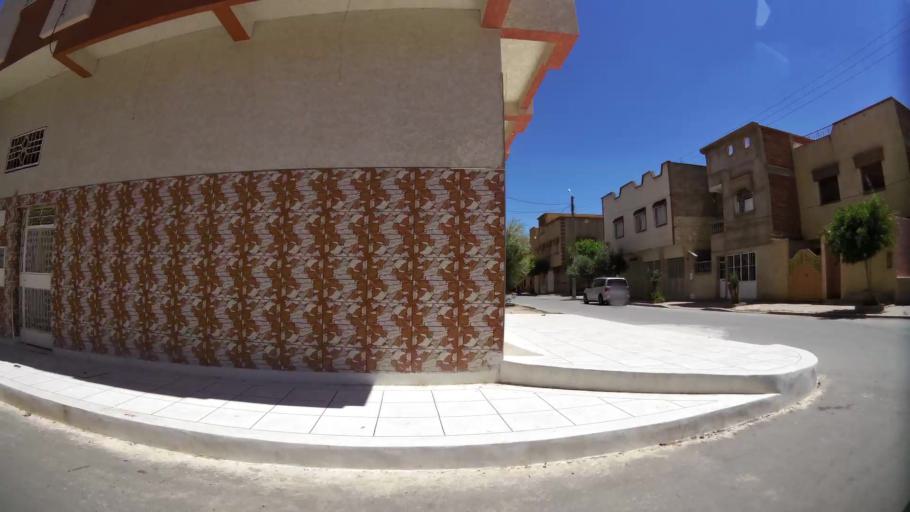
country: MA
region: Oriental
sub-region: Oujda-Angad
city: Oujda
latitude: 34.6588
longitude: -1.9237
